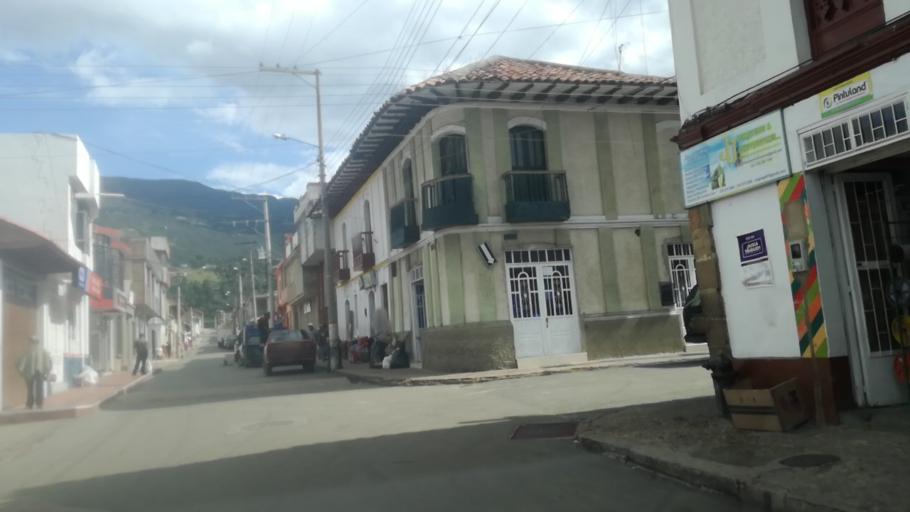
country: CO
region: Boyaca
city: Socha Viejo
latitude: 5.9972
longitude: -72.6928
